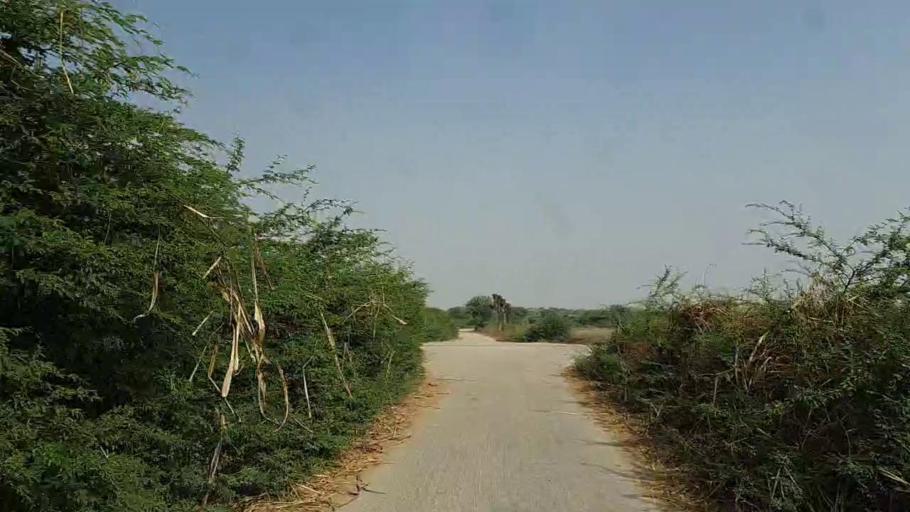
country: PK
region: Sindh
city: Naukot
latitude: 24.7675
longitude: 69.3589
